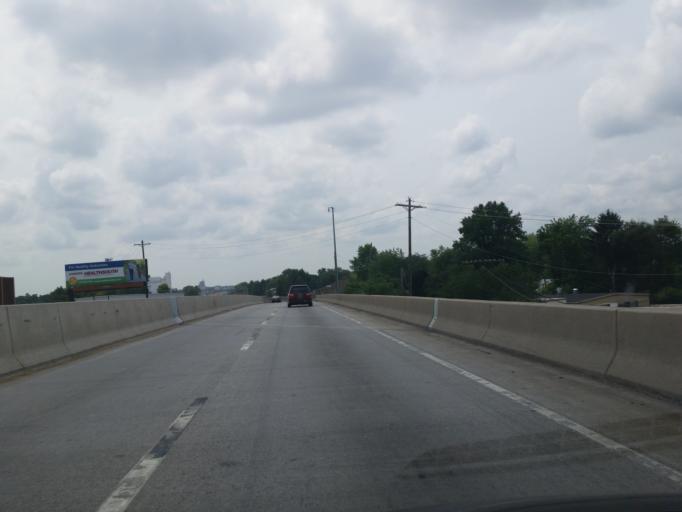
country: US
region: Pennsylvania
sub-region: Cumberland County
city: Camp Hill
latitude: 40.2350
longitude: -76.9121
